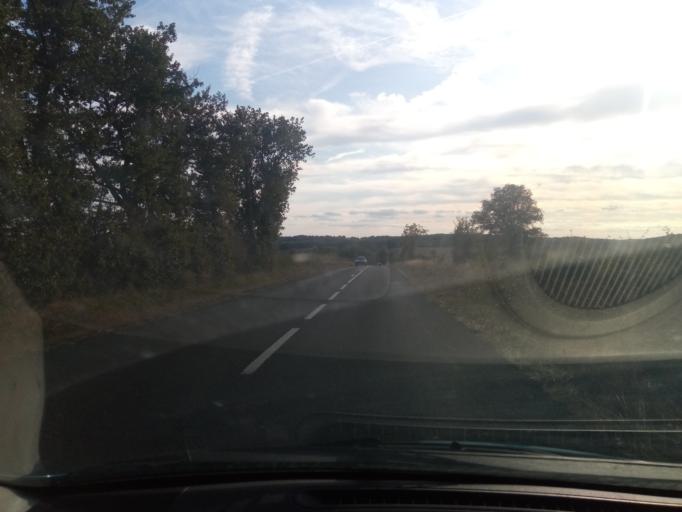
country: FR
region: Poitou-Charentes
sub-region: Departement de la Vienne
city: Montmorillon
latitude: 46.4972
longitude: 0.8427
